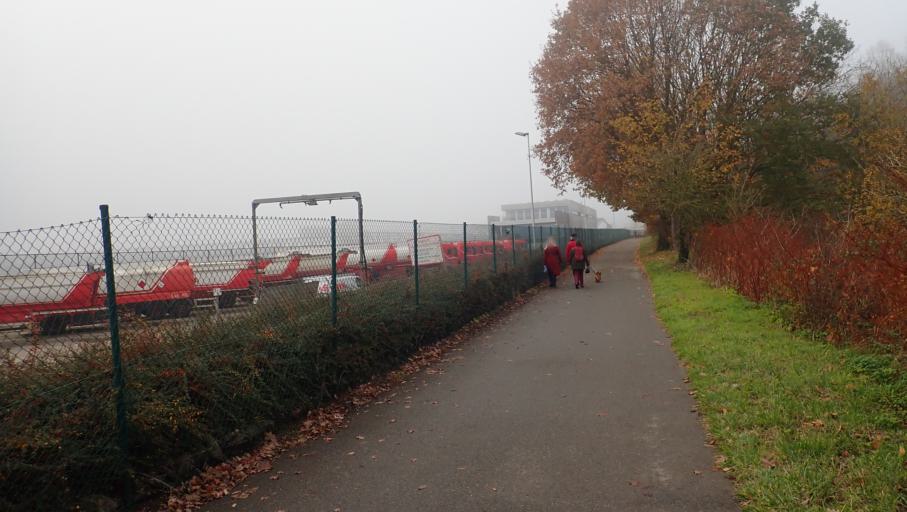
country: BE
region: Flanders
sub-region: Provincie Oost-Vlaanderen
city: Temse
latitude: 51.1226
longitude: 4.2242
